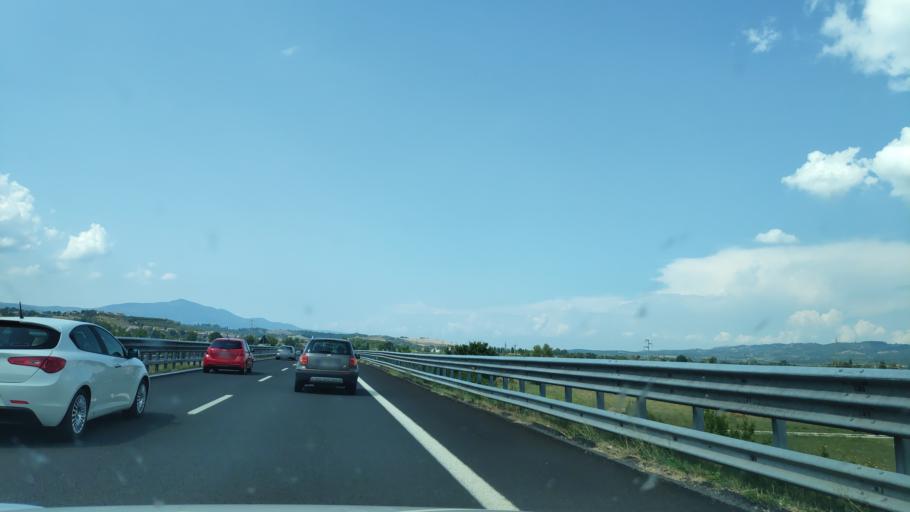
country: IT
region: Umbria
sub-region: Provincia di Terni
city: Fabro Scalo
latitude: 42.8628
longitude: 12.0352
